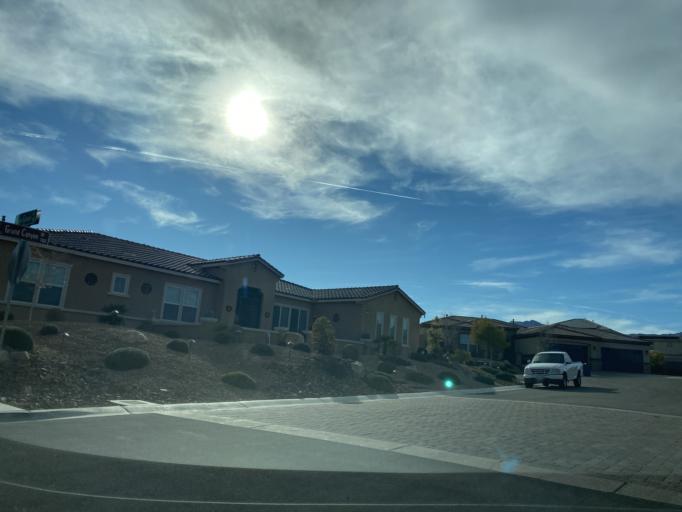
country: US
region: Nevada
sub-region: Clark County
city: Summerlin South
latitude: 36.2907
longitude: -115.3060
